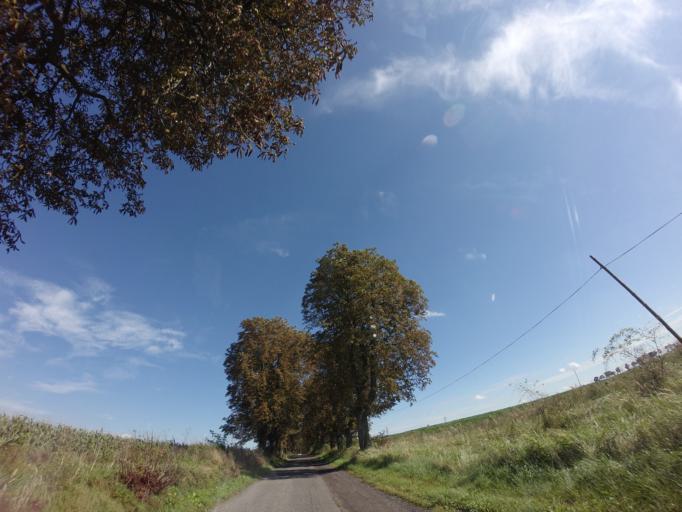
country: PL
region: West Pomeranian Voivodeship
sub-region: Powiat choszczenski
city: Recz
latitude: 53.2566
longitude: 15.5994
